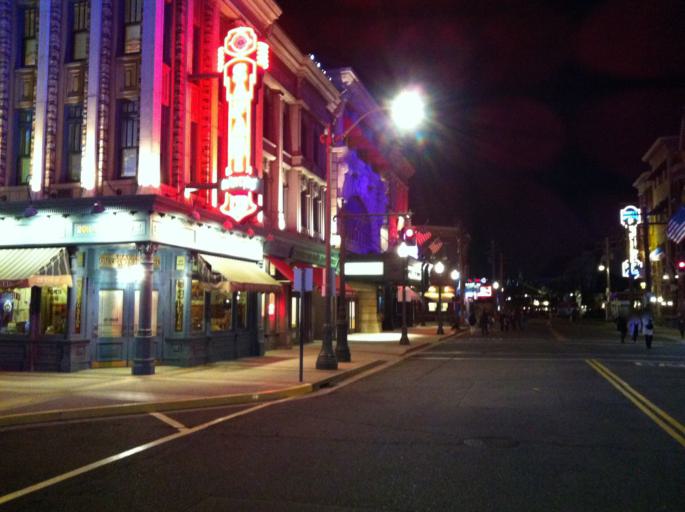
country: JP
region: Hyogo
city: Amagasaki
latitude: 34.6642
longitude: 135.4337
